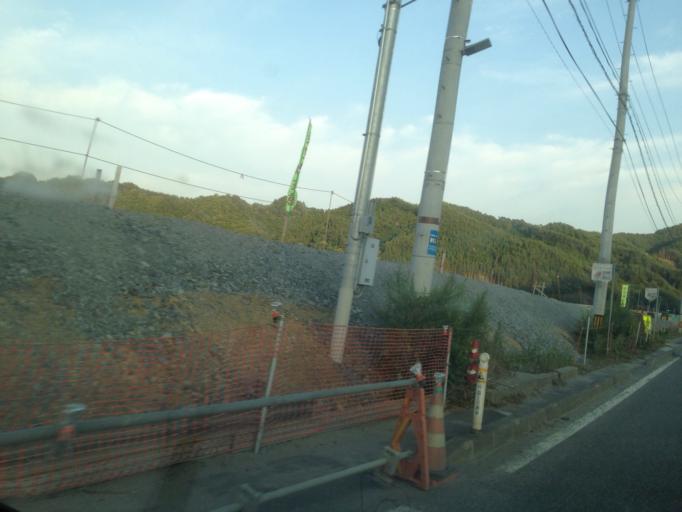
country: JP
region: Iwate
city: Otsuchi
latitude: 39.3294
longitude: 141.8848
